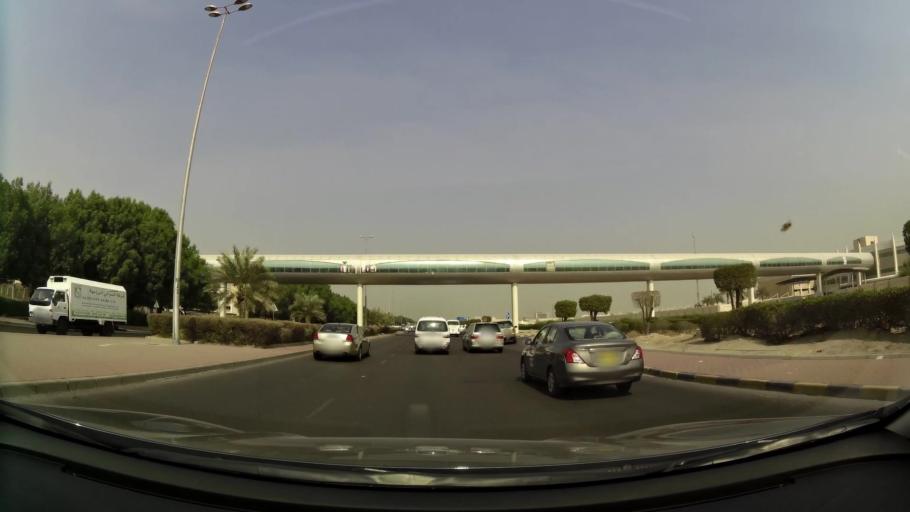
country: KW
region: Al Asimah
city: Ar Rabiyah
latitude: 29.2758
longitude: 47.9073
